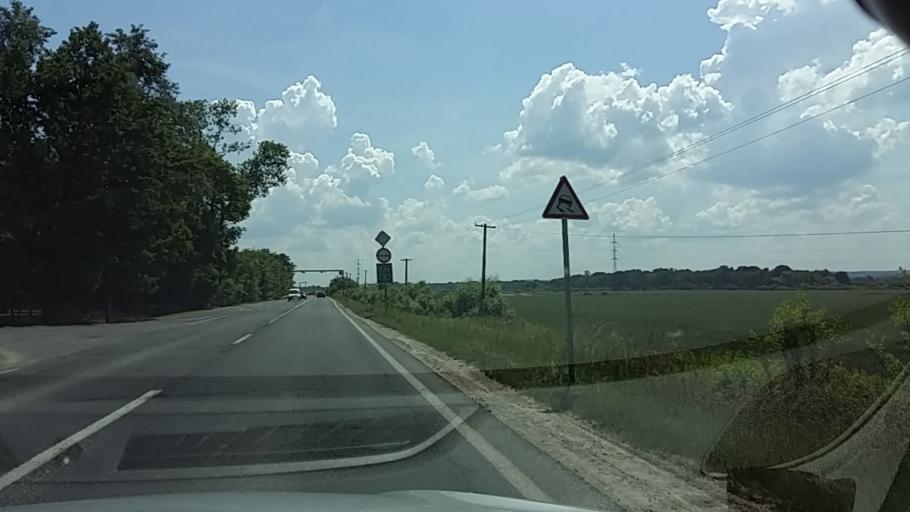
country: AT
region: Burgenland
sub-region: Politischer Bezirk Gussing
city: Heiligenbrunn
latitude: 46.9747
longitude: 16.3775
